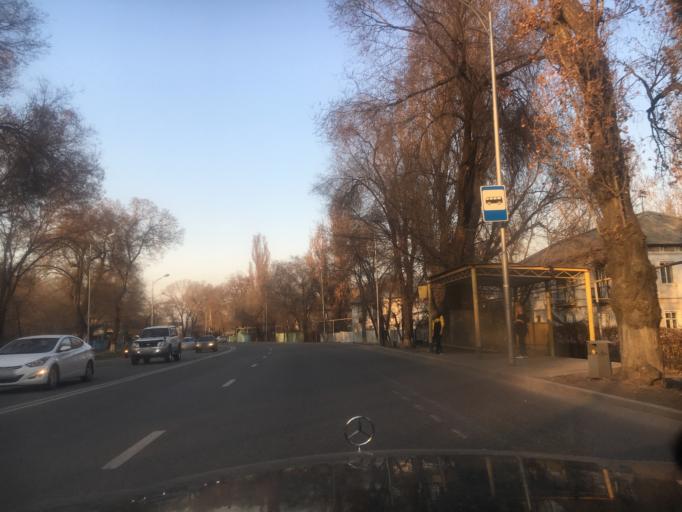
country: KZ
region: Almaty Oblysy
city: Pervomayskiy
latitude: 43.3540
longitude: 76.9759
